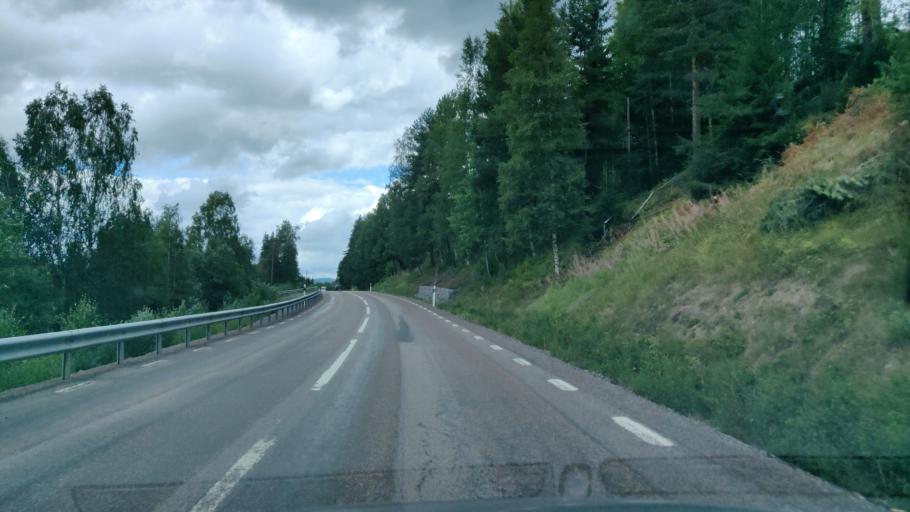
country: SE
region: Vaermland
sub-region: Torsby Kommun
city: Torsby
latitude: 60.5771
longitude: 13.0855
